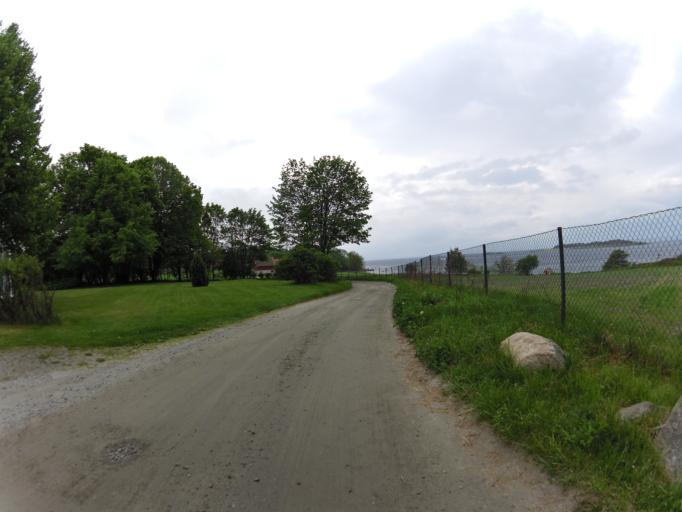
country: NO
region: Ostfold
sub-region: Moss
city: Moss
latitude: 59.4026
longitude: 10.6523
